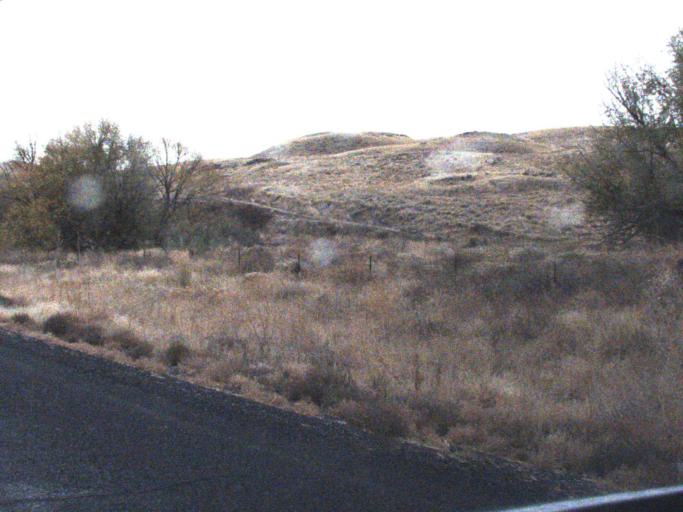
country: US
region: Washington
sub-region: Columbia County
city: Dayton
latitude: 46.7673
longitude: -118.0320
